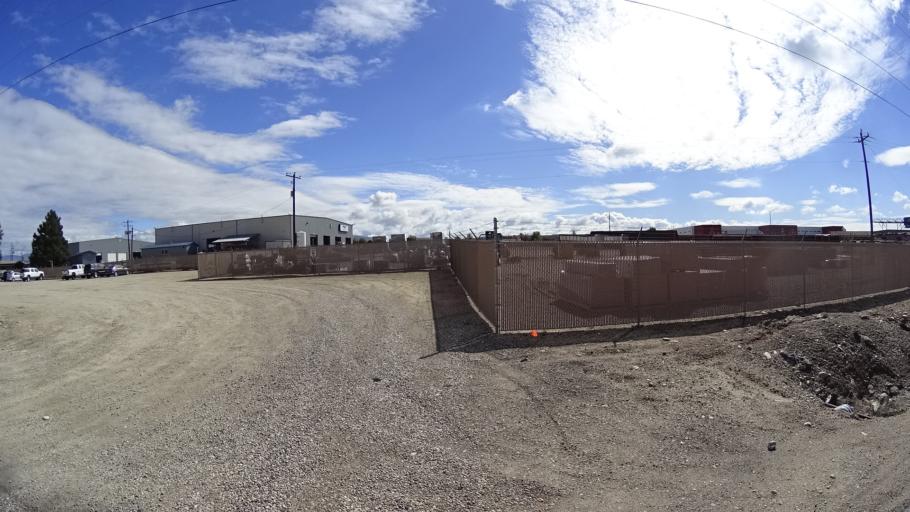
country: US
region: Idaho
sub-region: Ada County
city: Boise
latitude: 43.5254
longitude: -116.1541
